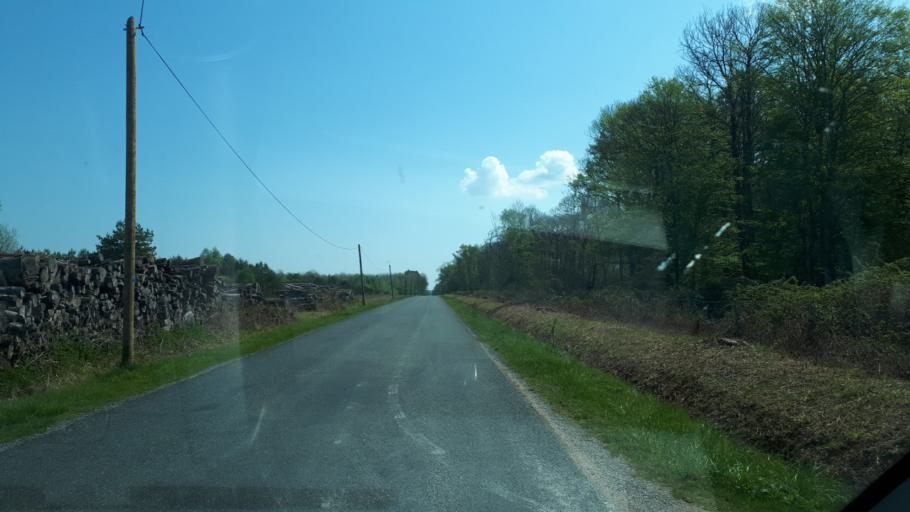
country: FR
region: Centre
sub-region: Departement du Cher
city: Neuvy-sur-Barangeon
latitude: 47.3190
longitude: 2.2093
